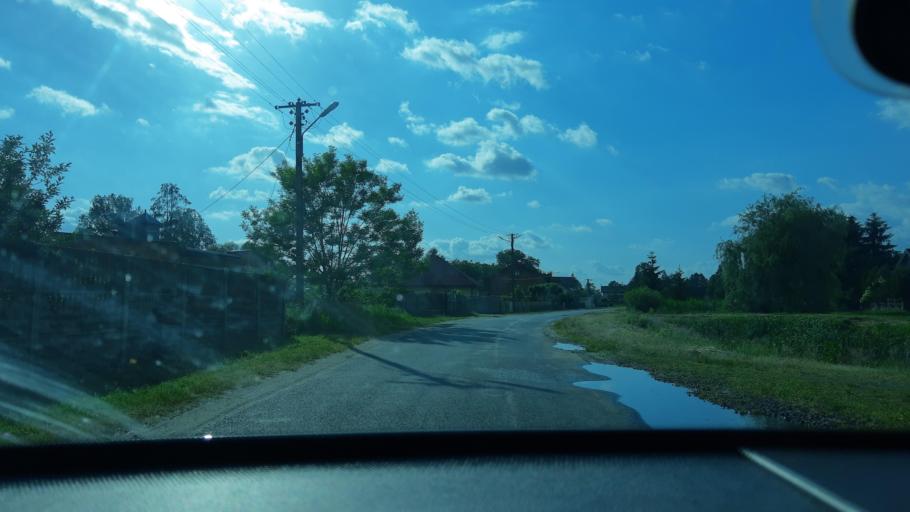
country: PL
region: Lodz Voivodeship
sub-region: Powiat zdunskowolski
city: Zapolice
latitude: 51.5257
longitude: 18.8412
